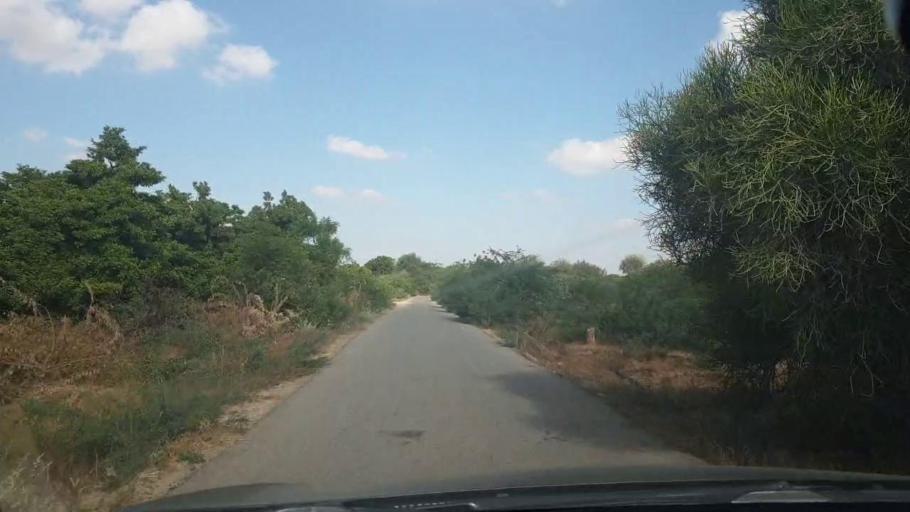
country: PK
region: Sindh
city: Malir Cantonment
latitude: 25.0573
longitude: 67.3911
